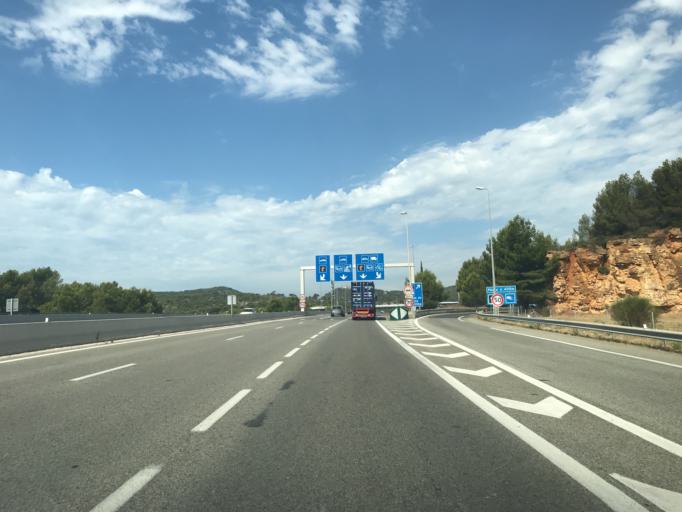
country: FR
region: Provence-Alpes-Cote d'Azur
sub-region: Departement des Bouches-du-Rhone
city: La Ciotat
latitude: 43.2037
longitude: 5.5951
